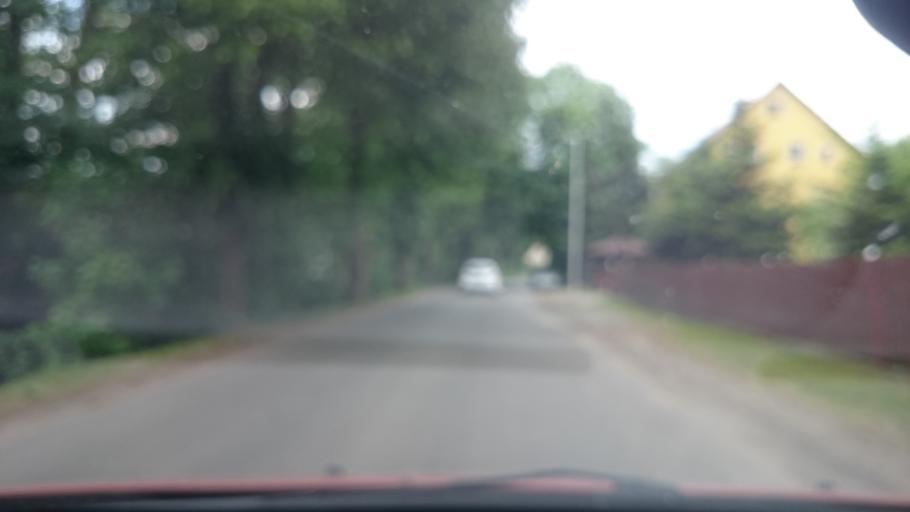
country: PL
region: Lower Silesian Voivodeship
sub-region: Powiat klodzki
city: Bystrzyca Klodzka
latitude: 50.3044
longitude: 16.6156
